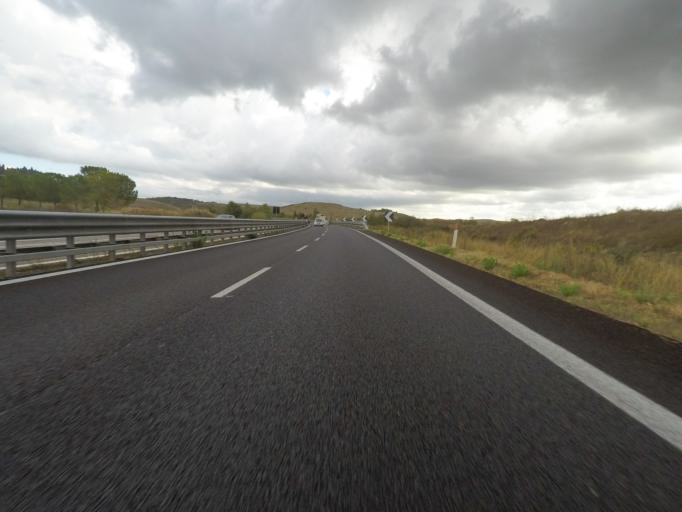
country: IT
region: Tuscany
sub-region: Provincia di Siena
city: Castelnuovo Berardenga
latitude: 43.3094
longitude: 11.4677
